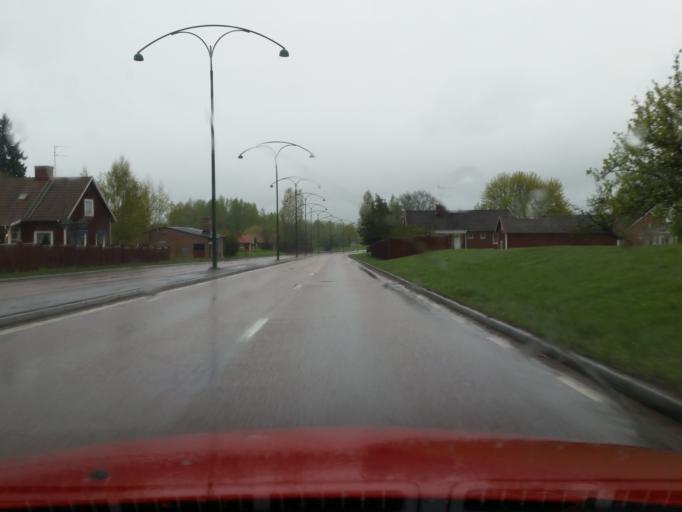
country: SE
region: Dalarna
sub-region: Borlange Kommun
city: Borlaenge
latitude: 60.4992
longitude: 15.3957
